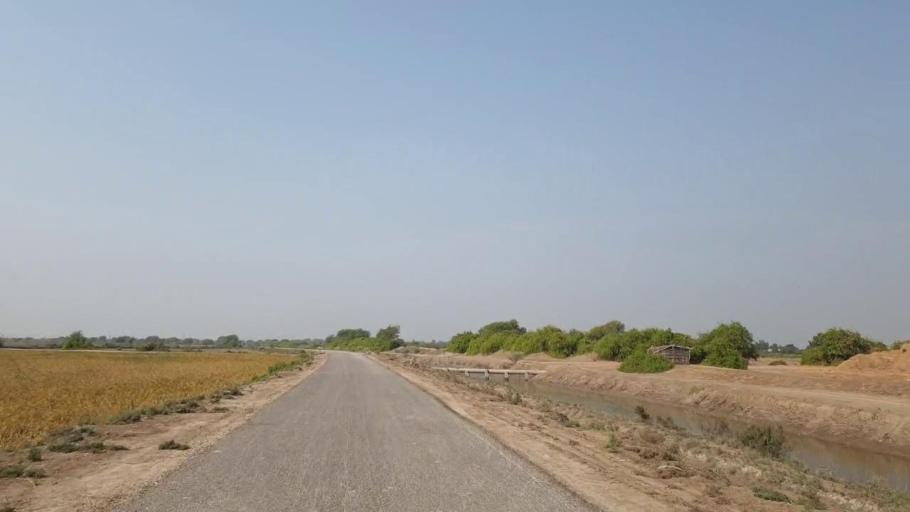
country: PK
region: Sindh
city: Matli
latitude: 24.9553
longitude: 68.5261
